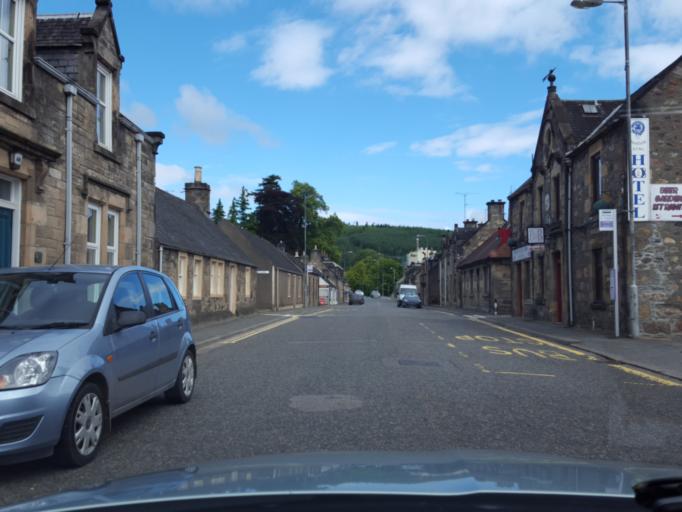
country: GB
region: Scotland
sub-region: Moray
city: Rothes
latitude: 57.5295
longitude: -3.2082
